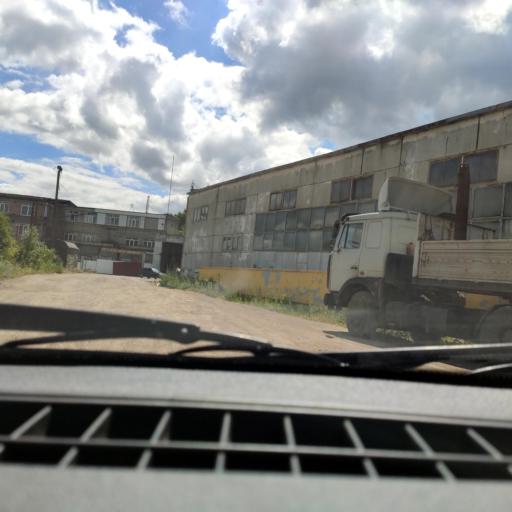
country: RU
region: Bashkortostan
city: Ufa
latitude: 54.8377
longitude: 56.1148
